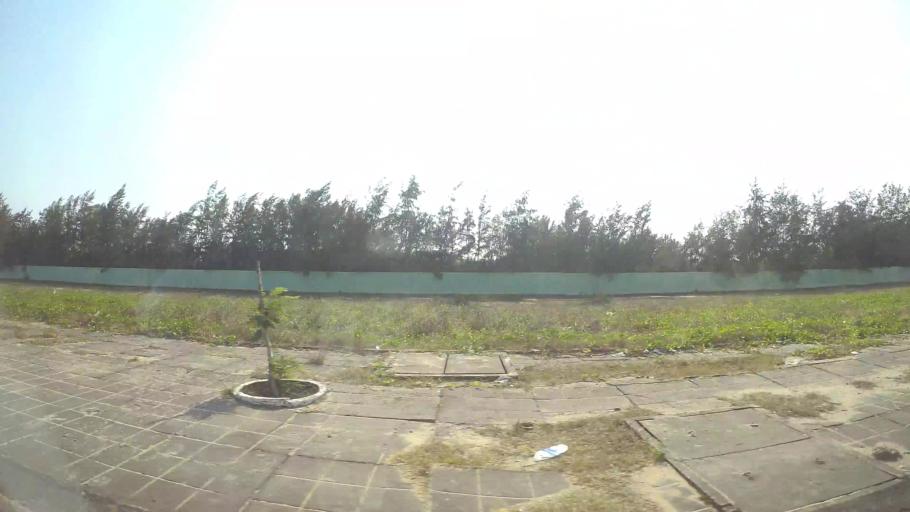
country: VN
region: Da Nang
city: Ngu Hanh Son
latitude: 15.9615
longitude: 108.2887
